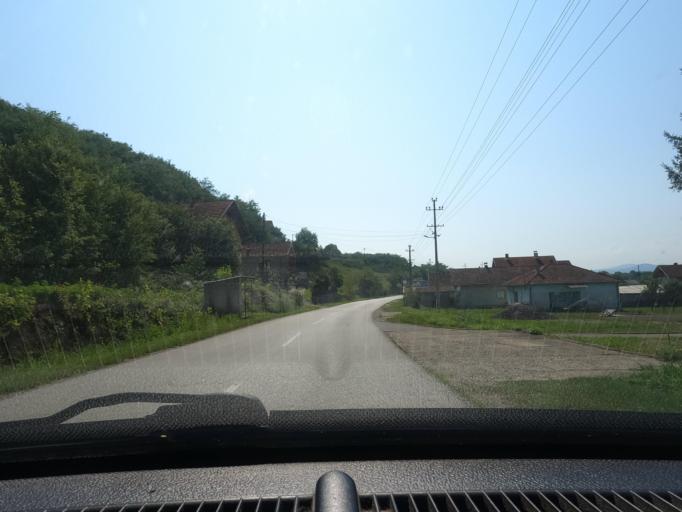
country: RS
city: Jadranska Lesnica
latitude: 44.5502
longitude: 19.3397
